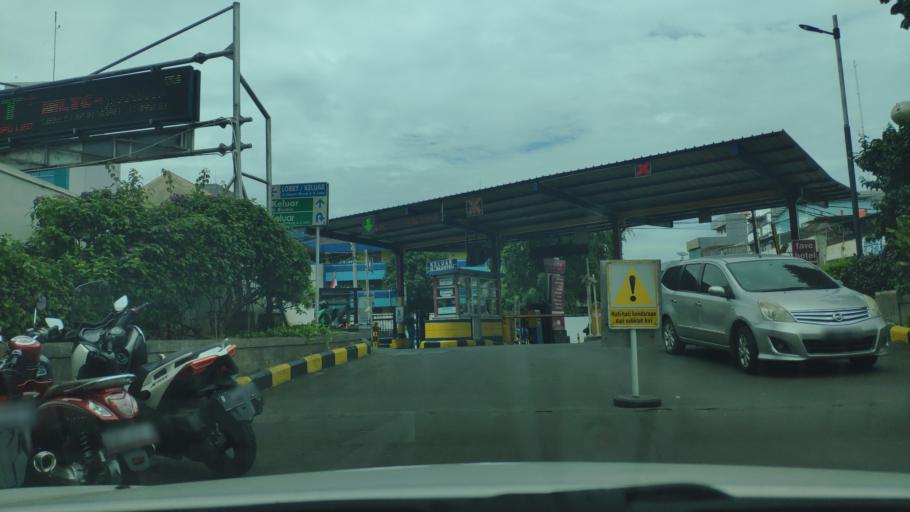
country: ID
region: Jakarta Raya
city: Jakarta
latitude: -6.1456
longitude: 106.8179
